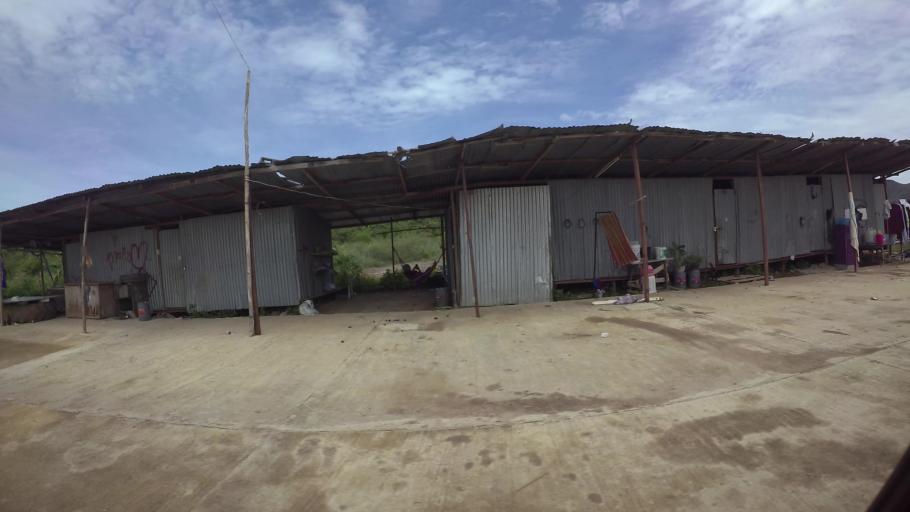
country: TH
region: Chon Buri
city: Sattahip
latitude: 12.6927
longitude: 100.8843
